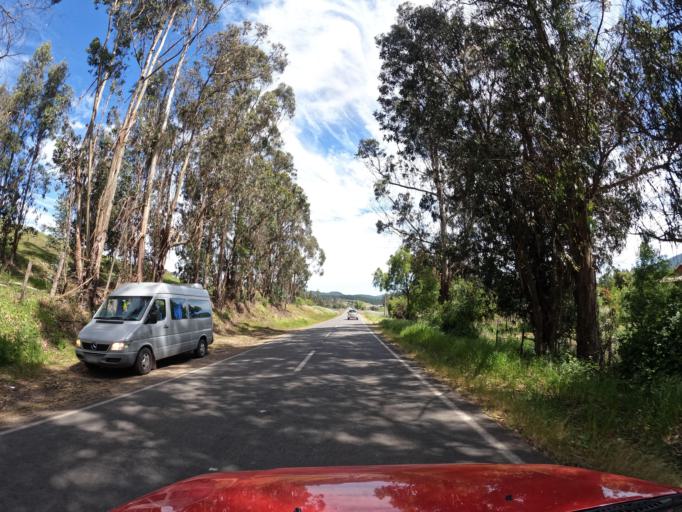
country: CL
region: Maule
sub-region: Provincia de Talca
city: Constitucion
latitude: -35.0118
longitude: -72.0365
